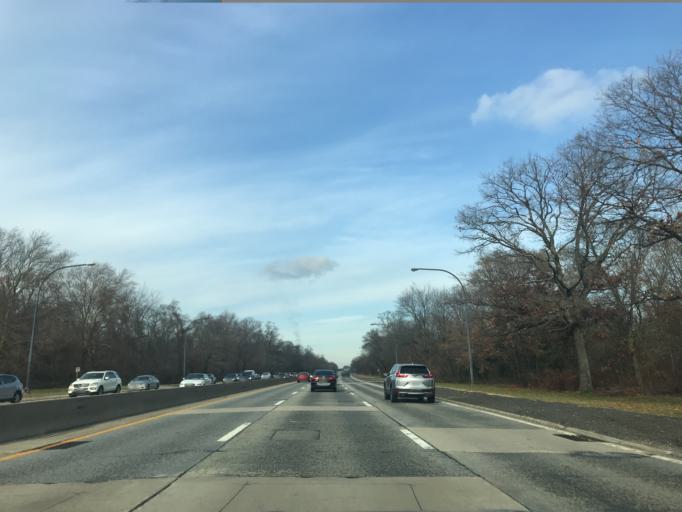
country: US
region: New York
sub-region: Nassau County
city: North Merrick
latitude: 40.6946
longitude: -73.5760
